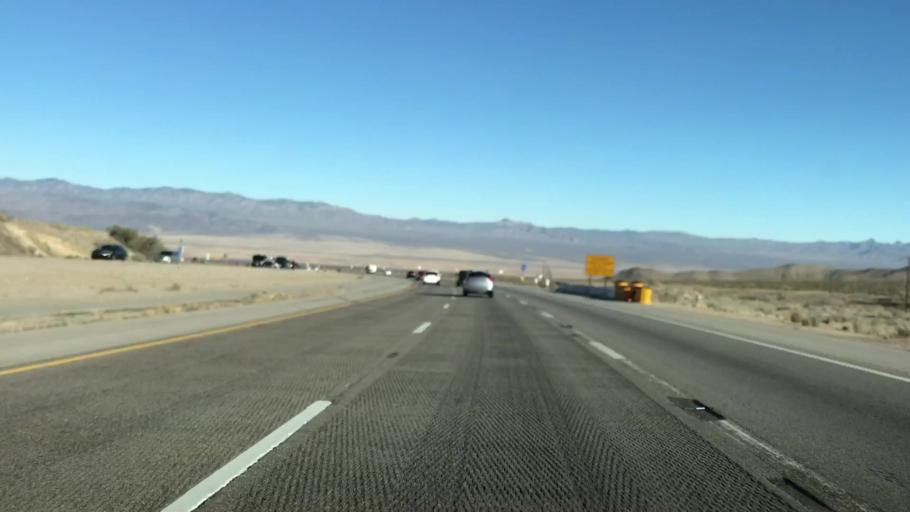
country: US
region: Nevada
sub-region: Clark County
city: Sandy Valley
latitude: 35.4609
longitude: -115.4703
